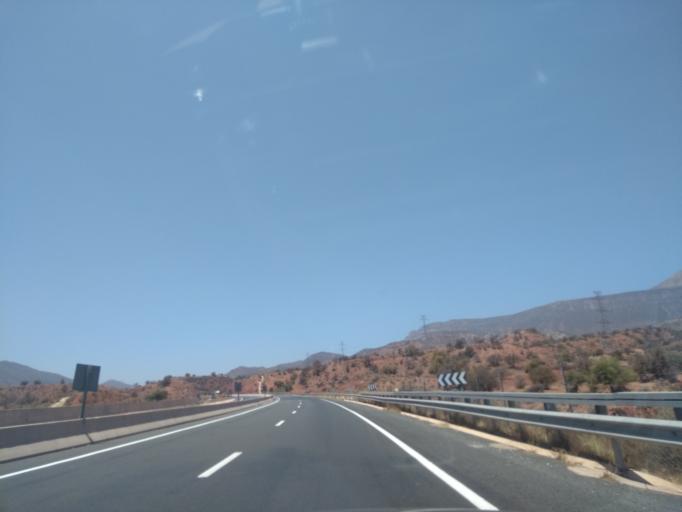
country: MA
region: Souss-Massa-Draa
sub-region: Taroudannt
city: Bigoudine
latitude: 30.6872
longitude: -9.2382
